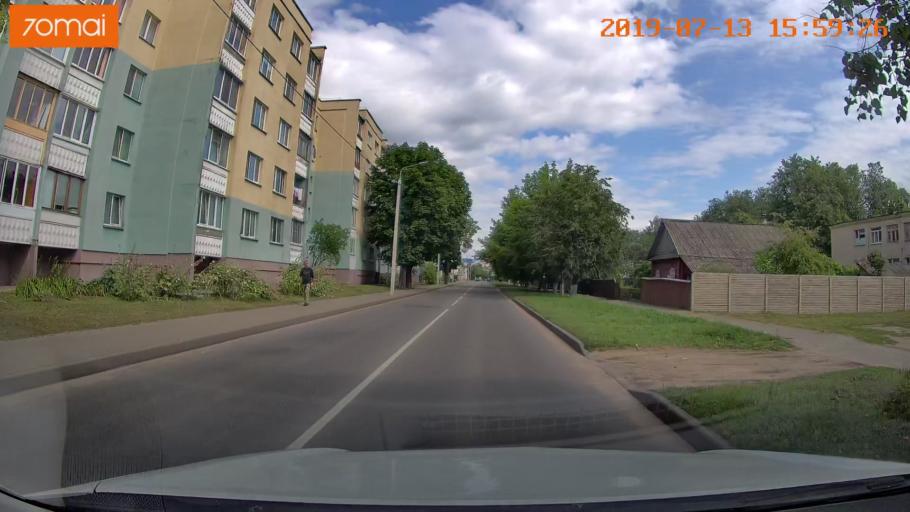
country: BY
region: Mogilev
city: Babruysk
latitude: 53.1457
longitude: 29.2153
